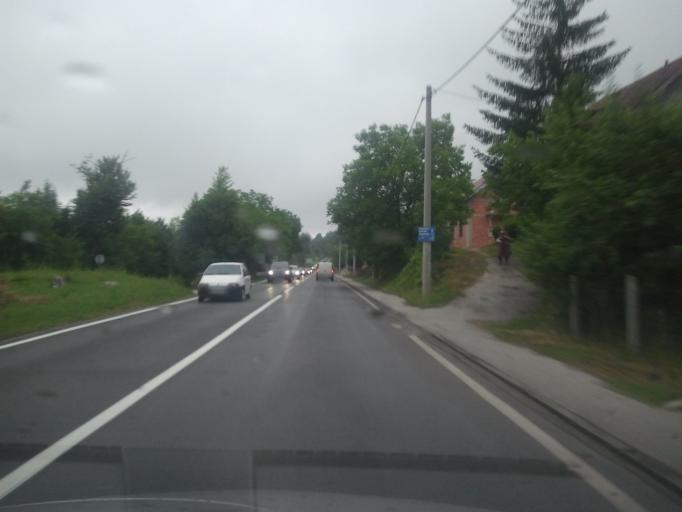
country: HR
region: Karlovacka
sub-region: Grad Karlovac
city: Slunj
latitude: 45.1073
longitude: 15.5860
